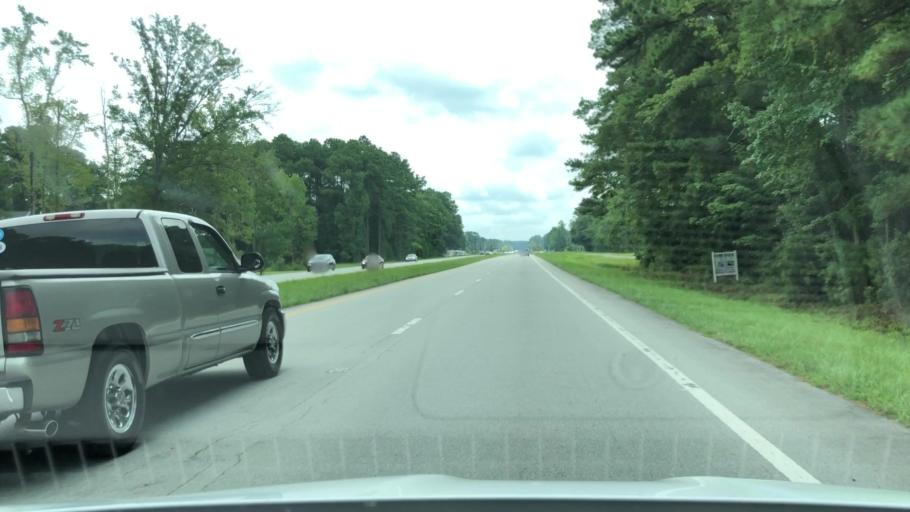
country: US
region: North Carolina
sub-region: Craven County
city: Fairfield Harbour
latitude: 35.0180
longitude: -76.9965
